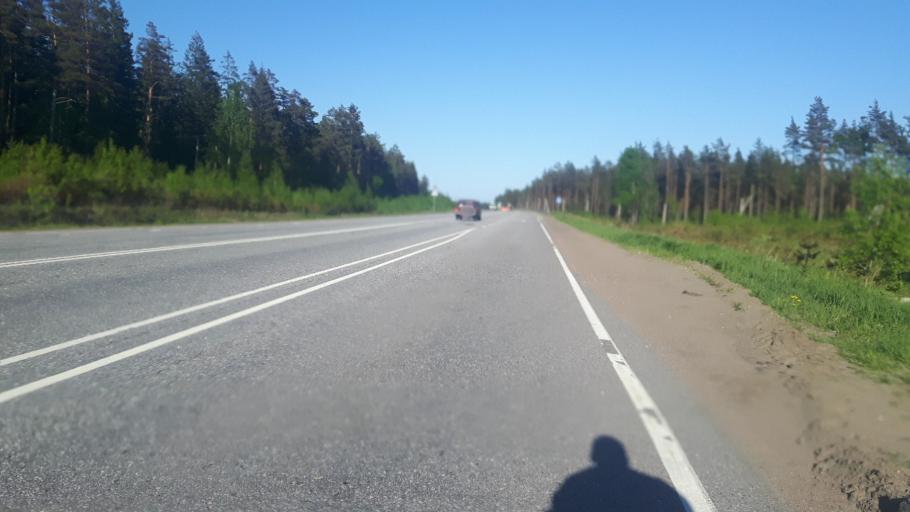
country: RU
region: Leningrad
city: Molodezhnoye
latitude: 60.1717
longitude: 29.3121
